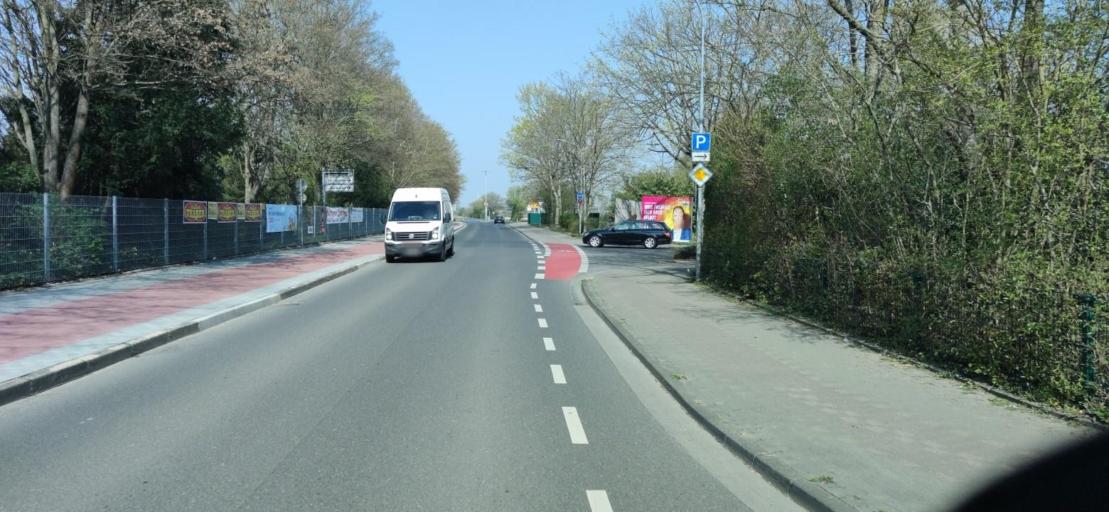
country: DE
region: North Rhine-Westphalia
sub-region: Regierungsbezirk Dusseldorf
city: Kaarst
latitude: 51.2012
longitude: 6.6045
